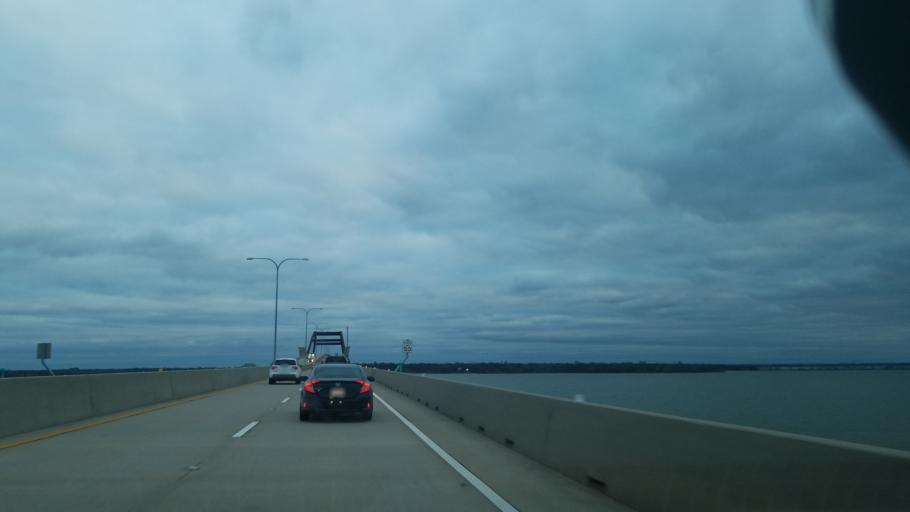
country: US
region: Texas
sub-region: Denton County
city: Lake Dallas
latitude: 33.1393
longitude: -97.0080
